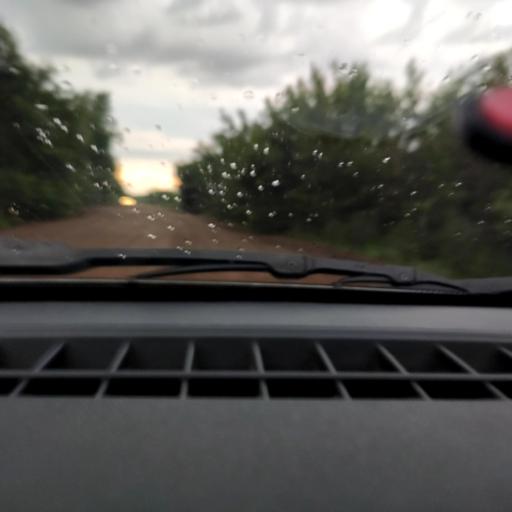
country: RU
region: Bashkortostan
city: Blagoveshchensk
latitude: 54.9256
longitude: 55.9710
